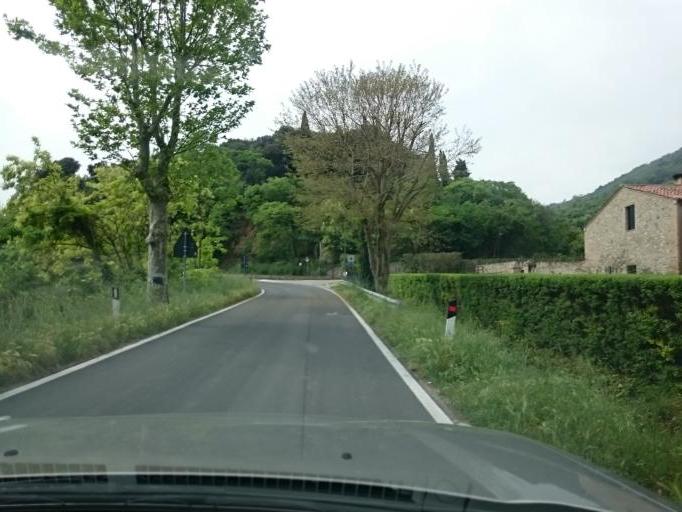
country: IT
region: Veneto
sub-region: Provincia di Padova
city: Arqua Petrarca
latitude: 45.2695
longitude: 11.7300
